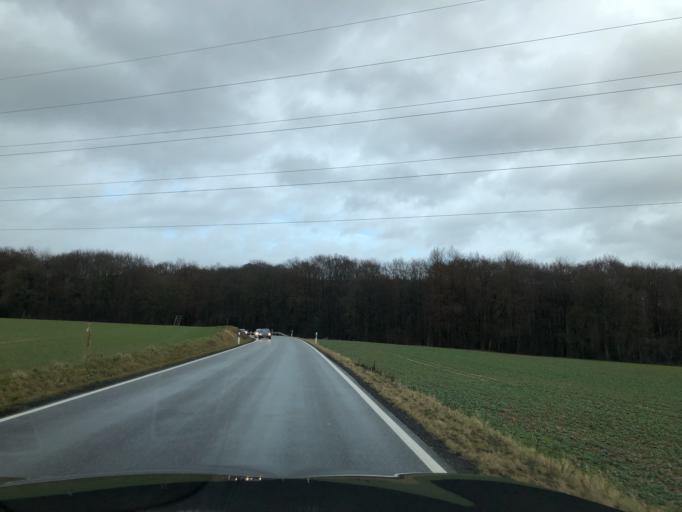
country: DE
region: Rheinland-Pfalz
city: Kasbach-Ohlenberg
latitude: 50.6020
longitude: 7.2728
